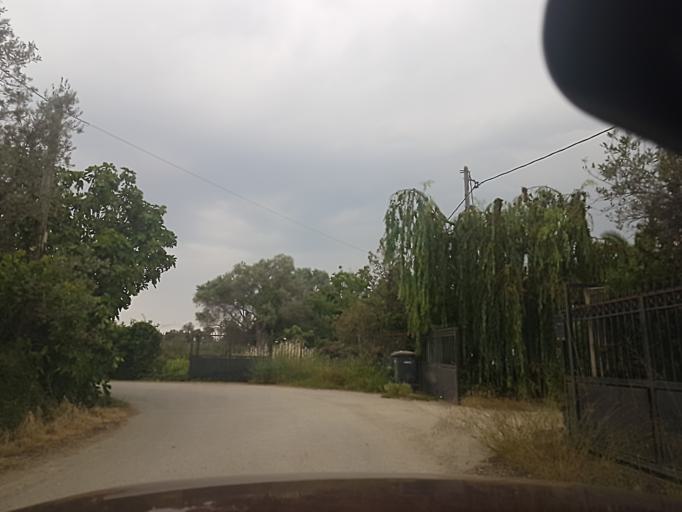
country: GR
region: Central Greece
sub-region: Nomos Evvoias
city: Mytikas
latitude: 38.4501
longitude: 23.6539
